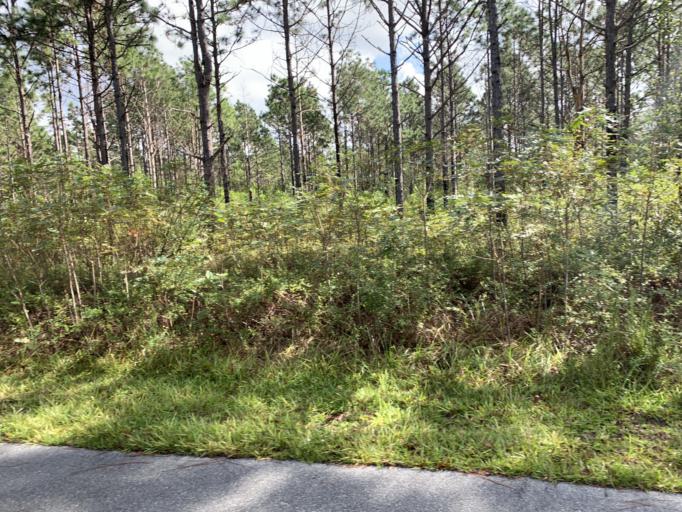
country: US
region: Florida
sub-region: Marion County
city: Silver Springs Shores
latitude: 29.1521
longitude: -82.0429
